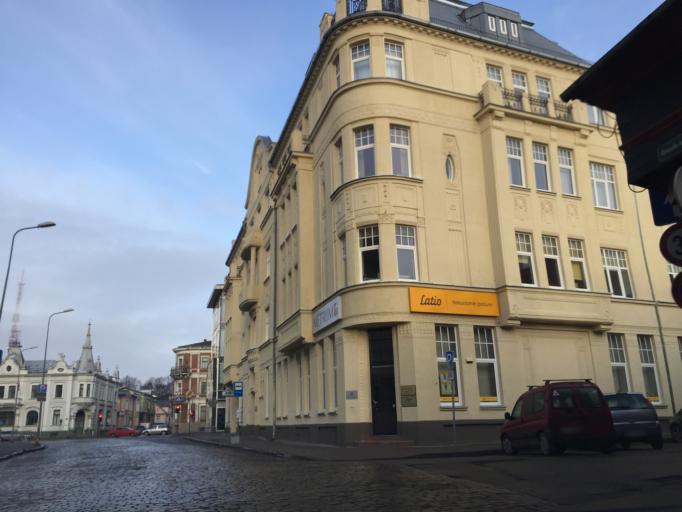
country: LV
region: Liepaja
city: Liepaja
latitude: 56.5102
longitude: 21.0066
